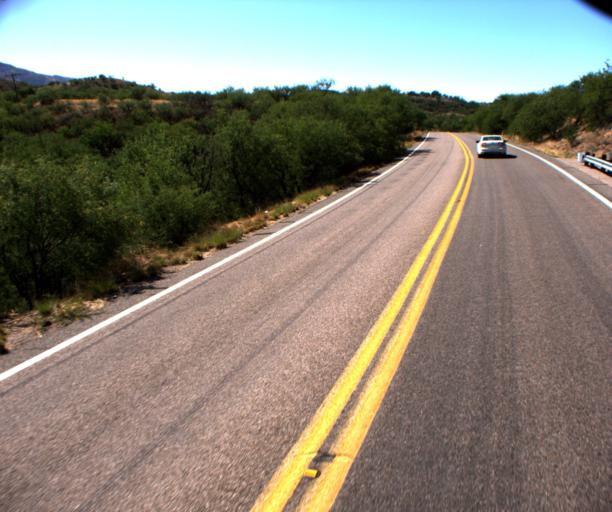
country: US
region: Arizona
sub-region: Santa Cruz County
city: Rio Rico
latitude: 31.5035
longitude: -110.8088
